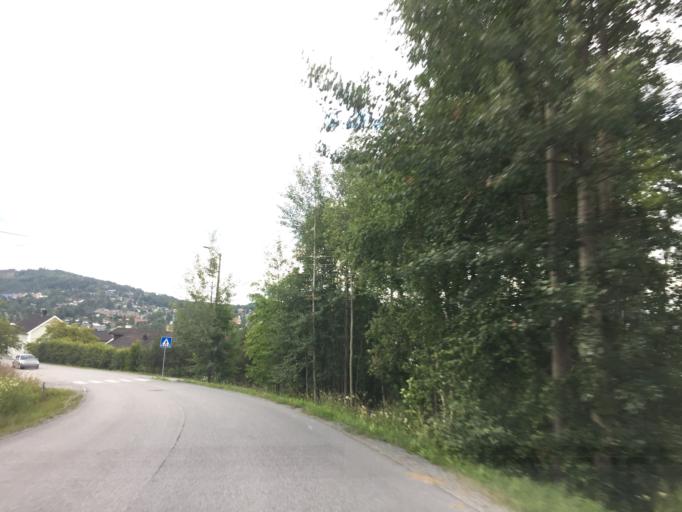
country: NO
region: Hedmark
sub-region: Kongsvinger
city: Kongsvinger
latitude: 60.1834
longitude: 11.9990
